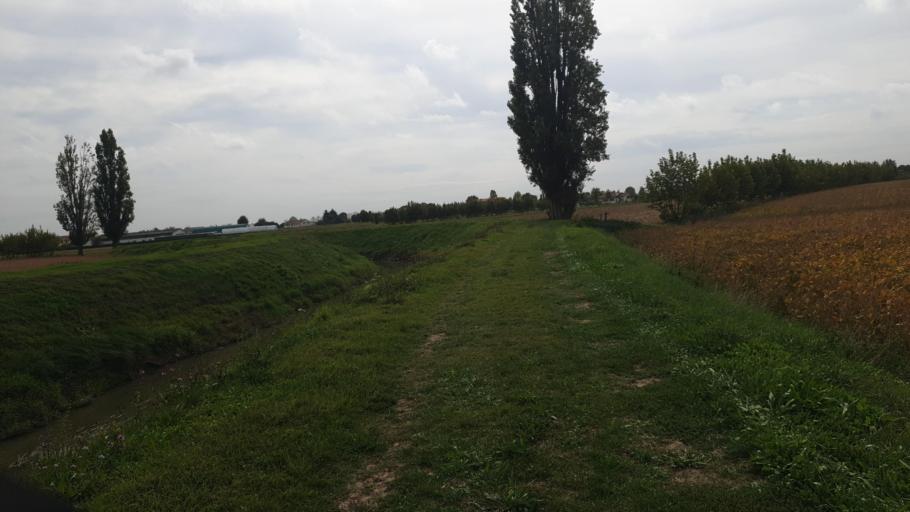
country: IT
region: Veneto
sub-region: Provincia di Padova
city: Casalserugo
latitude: 45.3347
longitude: 11.9250
